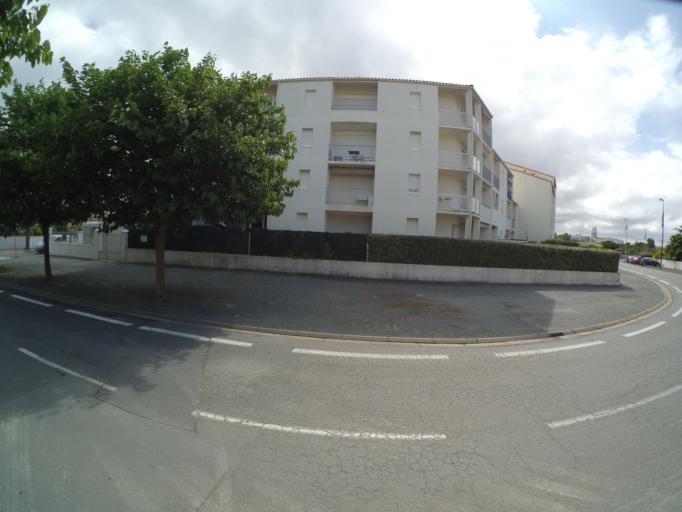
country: FR
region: Poitou-Charentes
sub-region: Departement de la Charente-Maritime
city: Chatelaillon-Plage
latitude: 46.0634
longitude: -1.0923
